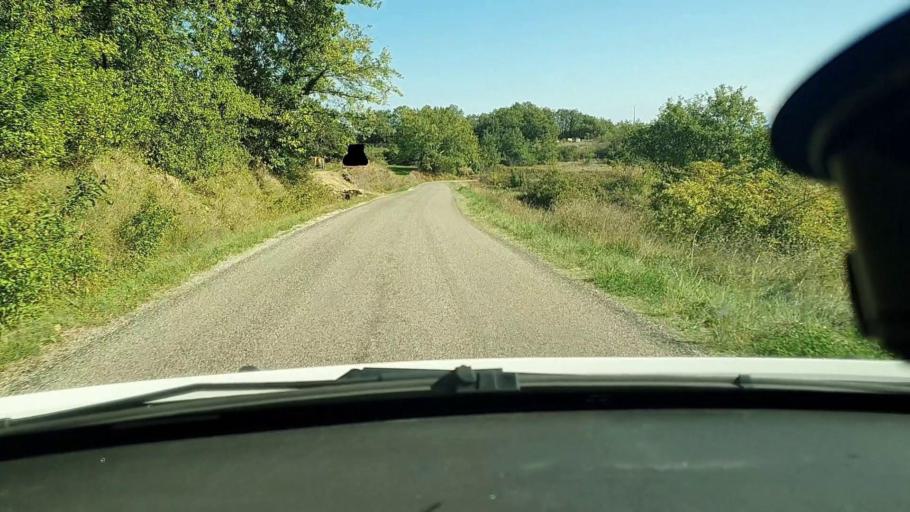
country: FR
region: Languedoc-Roussillon
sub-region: Departement du Gard
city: Saint-Julien-de-Peyrolas
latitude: 44.2633
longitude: 4.5287
